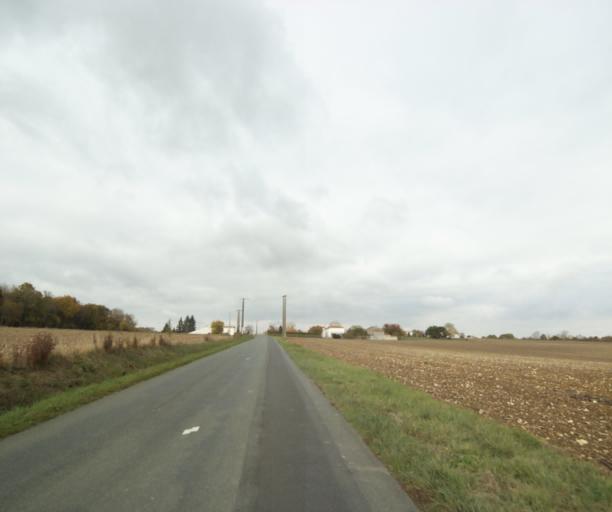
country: FR
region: Poitou-Charentes
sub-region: Departement de la Charente-Maritime
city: Saint-Georges-des-Coteaux
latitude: 45.7688
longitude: -0.6741
